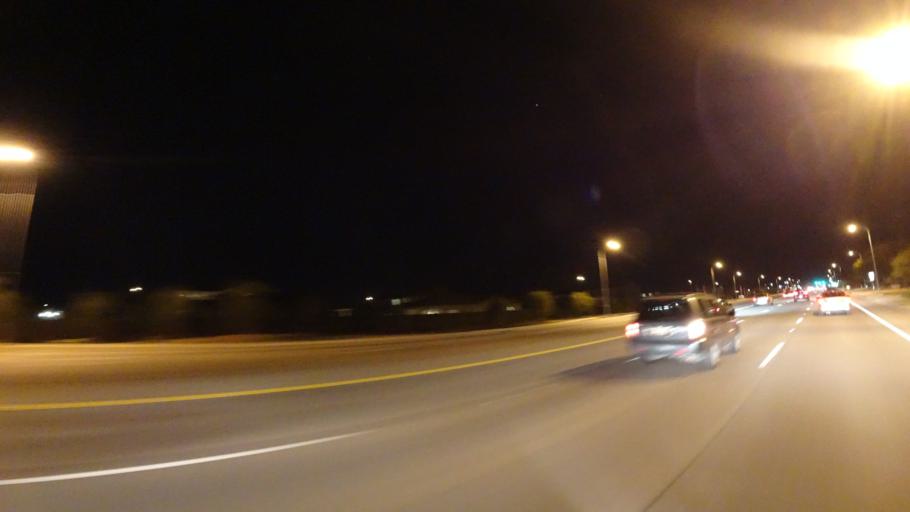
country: US
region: Arizona
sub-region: Maricopa County
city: Chandler
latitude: 33.2530
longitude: -111.7897
